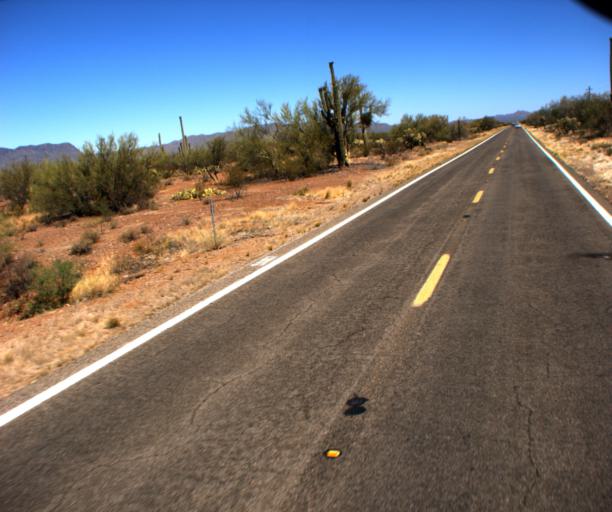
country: US
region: Arizona
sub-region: Pima County
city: Sells
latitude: 32.0456
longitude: -112.0217
